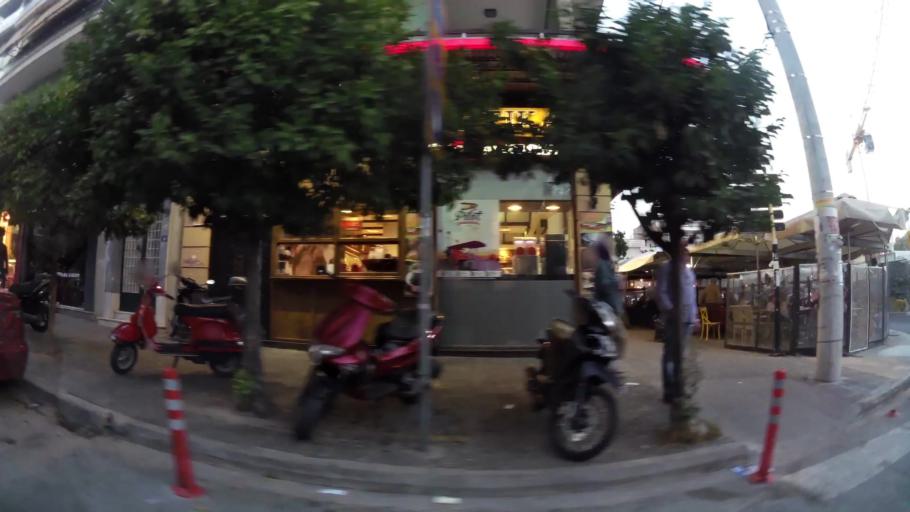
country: GR
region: Attica
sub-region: Nomos Piraios
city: Korydallos
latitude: 37.9771
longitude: 23.6497
